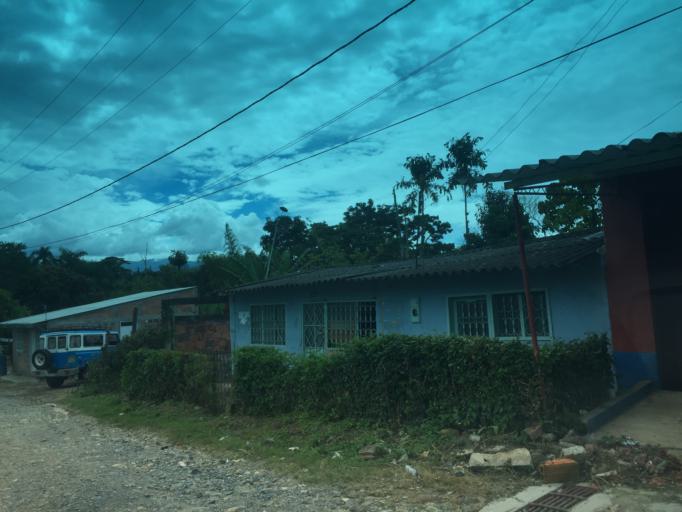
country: CO
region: Santander
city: Guepsa
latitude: 6.0183
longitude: -73.5483
